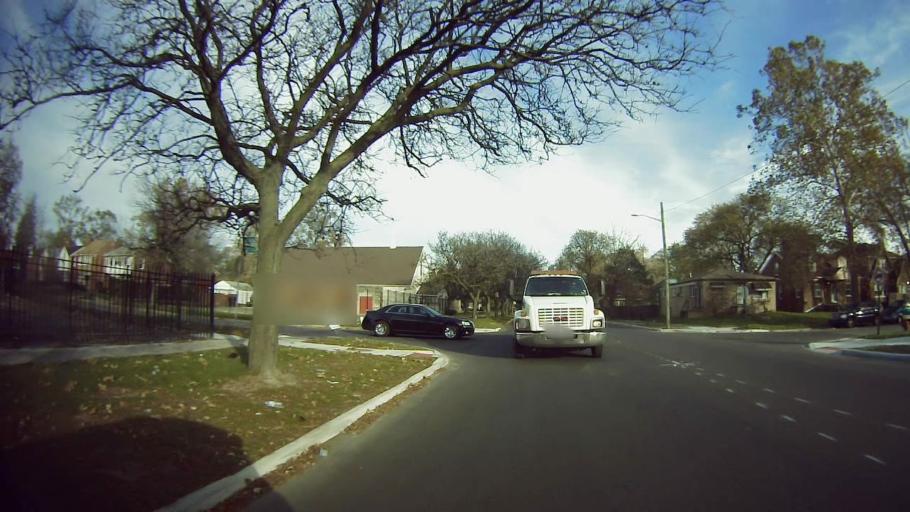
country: US
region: Michigan
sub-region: Oakland County
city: Oak Park
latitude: 42.4088
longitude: -83.1981
